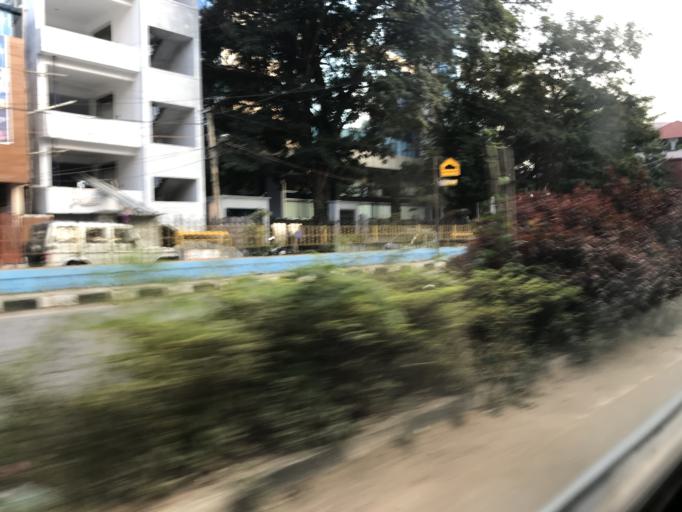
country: IN
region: Karnataka
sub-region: Bangalore Urban
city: Bangalore
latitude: 12.9938
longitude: 77.5892
